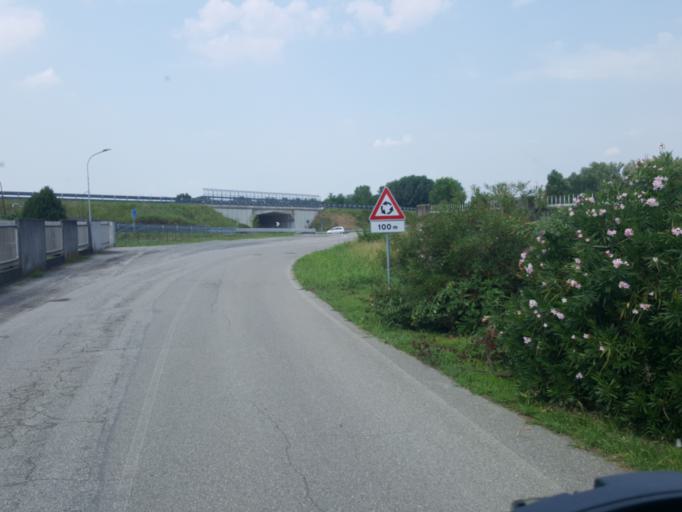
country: IT
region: Lombardy
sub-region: Provincia di Lodi
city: Guardamiglio
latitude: 45.1118
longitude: 9.6884
